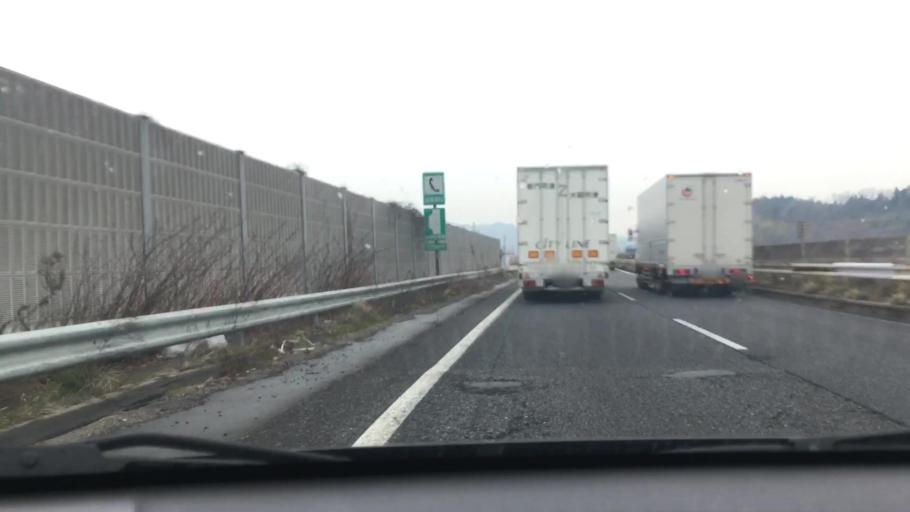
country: JP
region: Mie
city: Ueno-ebisumachi
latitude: 34.7789
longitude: 136.1578
